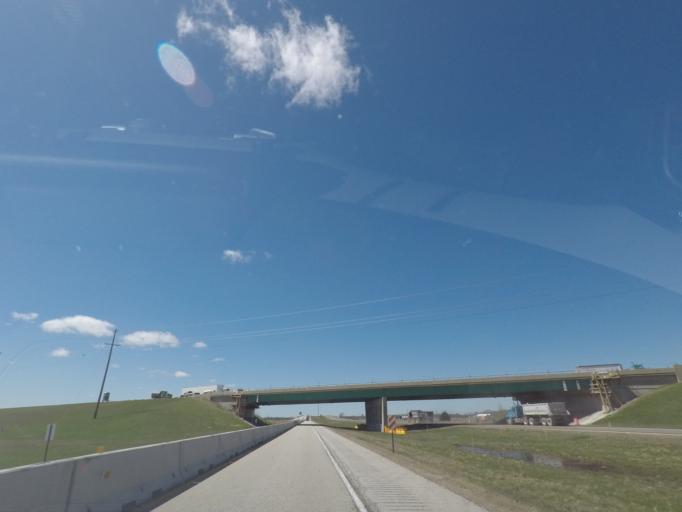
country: US
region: Illinois
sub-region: Livingston County
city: Pontiac
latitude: 40.9187
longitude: -88.6422
